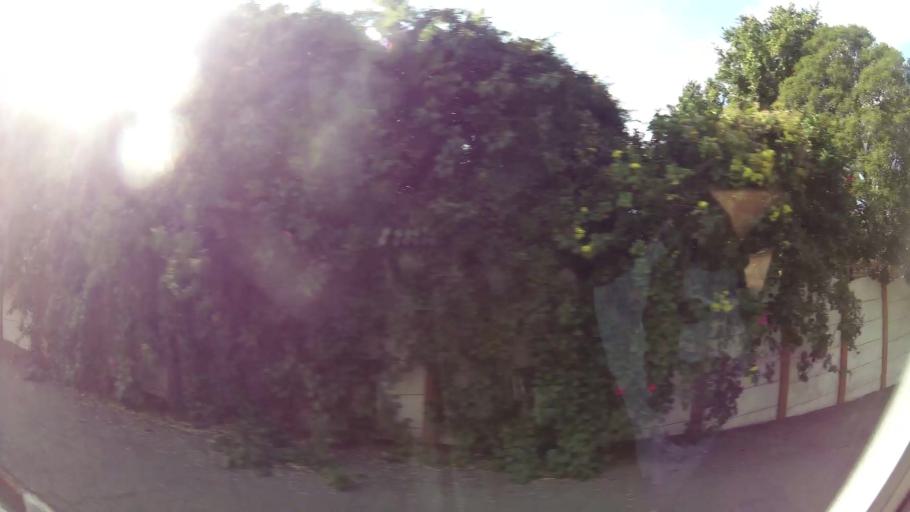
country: ZA
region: Gauteng
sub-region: Ekurhuleni Metropolitan Municipality
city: Germiston
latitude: -26.1757
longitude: 28.1776
